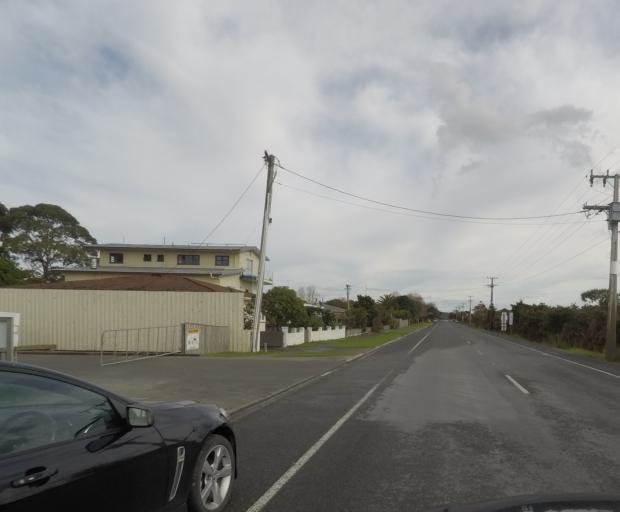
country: NZ
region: Northland
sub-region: Whangarei
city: Ruakaka
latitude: -35.9859
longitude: 174.4519
